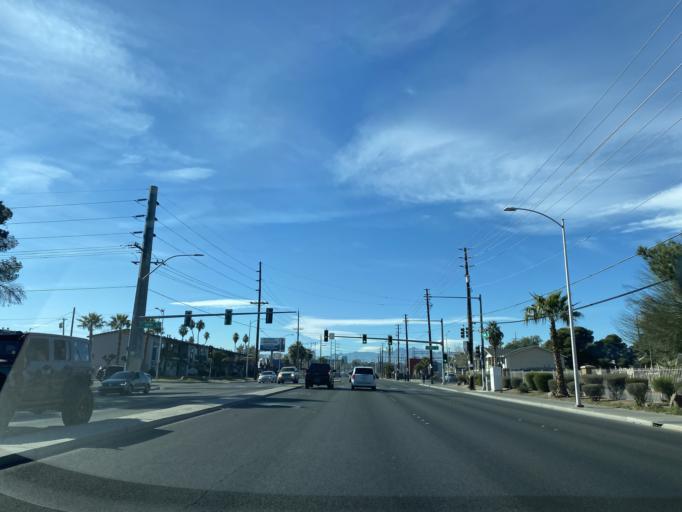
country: US
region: Nevada
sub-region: Clark County
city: North Las Vegas
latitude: 36.1738
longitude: -115.1111
